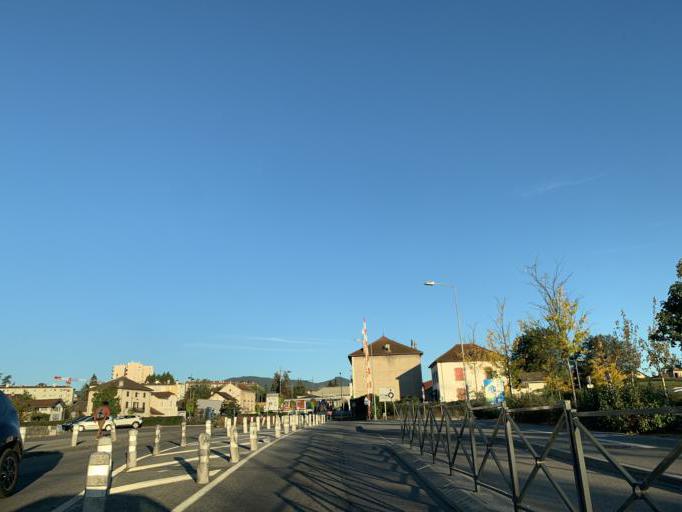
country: FR
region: Rhone-Alpes
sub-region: Departement de l'Ain
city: Belley
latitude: 45.7582
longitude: 5.6987
